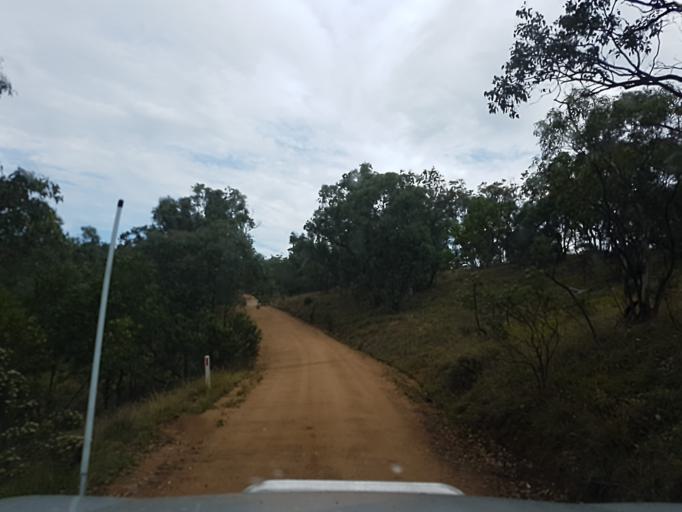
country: AU
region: New South Wales
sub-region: Snowy River
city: Jindabyne
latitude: -36.9416
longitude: 148.3460
